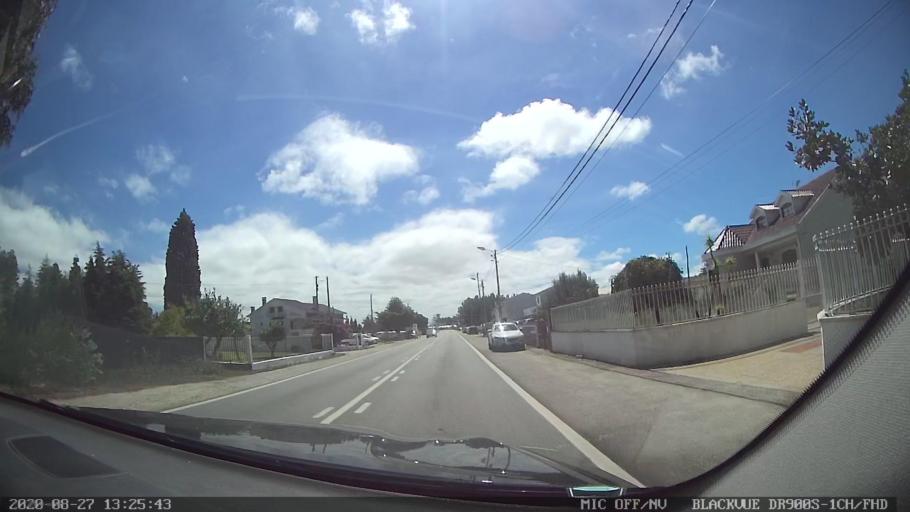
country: PT
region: Aveiro
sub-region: Vagos
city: Vagos
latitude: 40.5440
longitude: -8.6783
